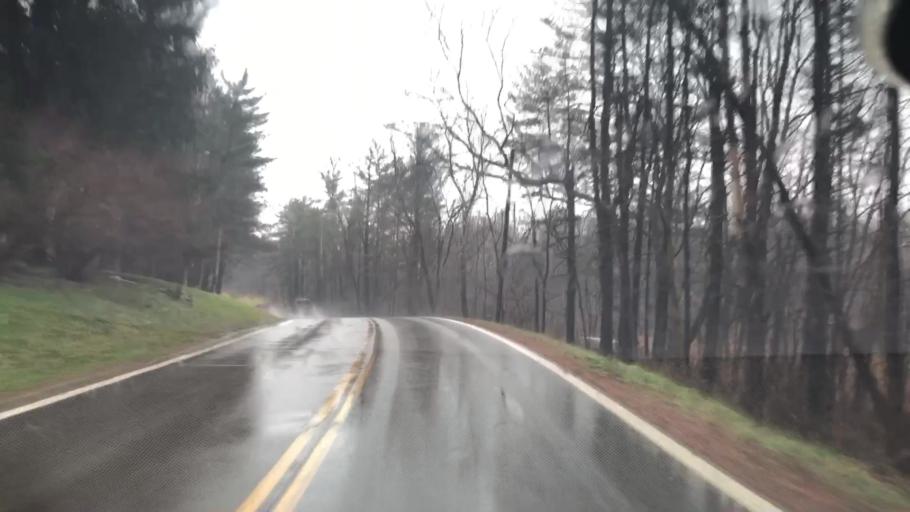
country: US
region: Ohio
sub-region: Harrison County
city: Cadiz
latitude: 40.1700
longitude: -80.9875
